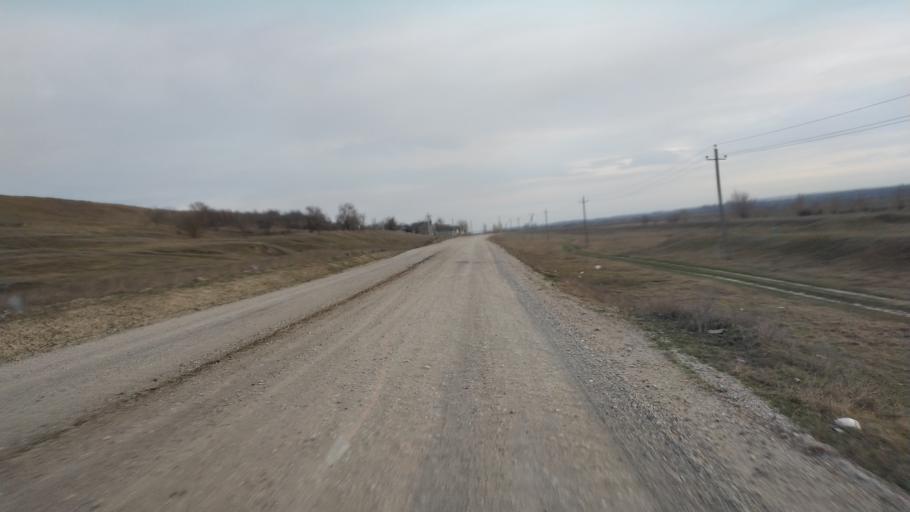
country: MD
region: Hincesti
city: Dancu
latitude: 46.7791
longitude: 28.1967
